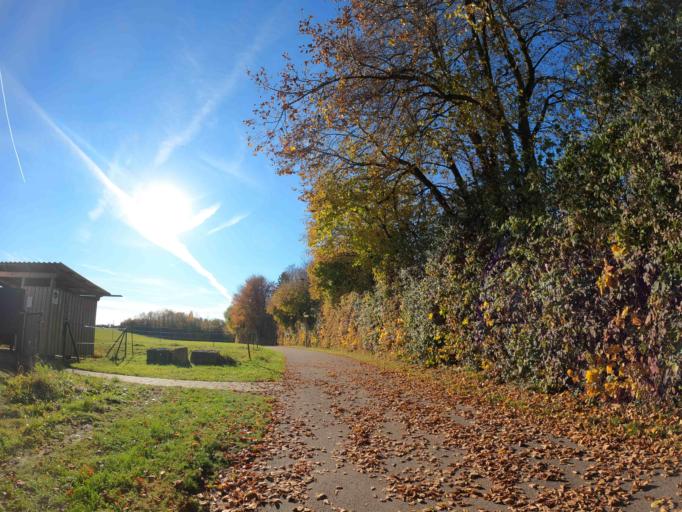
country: DE
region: Bavaria
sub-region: Upper Bavaria
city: Oberhaching
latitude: 48.0267
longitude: 11.6016
